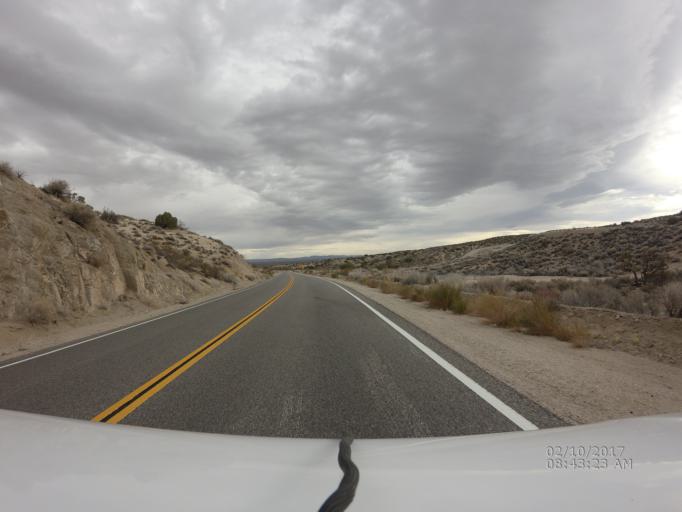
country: US
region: California
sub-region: Los Angeles County
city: Littlerock
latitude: 34.4784
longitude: -117.8993
